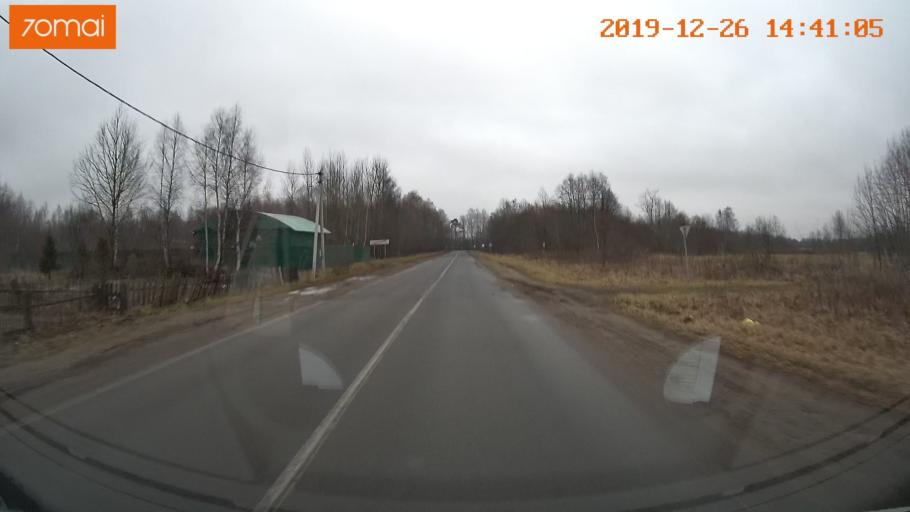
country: RU
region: Jaroslavl
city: Poshekhon'ye
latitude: 58.3727
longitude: 39.0121
